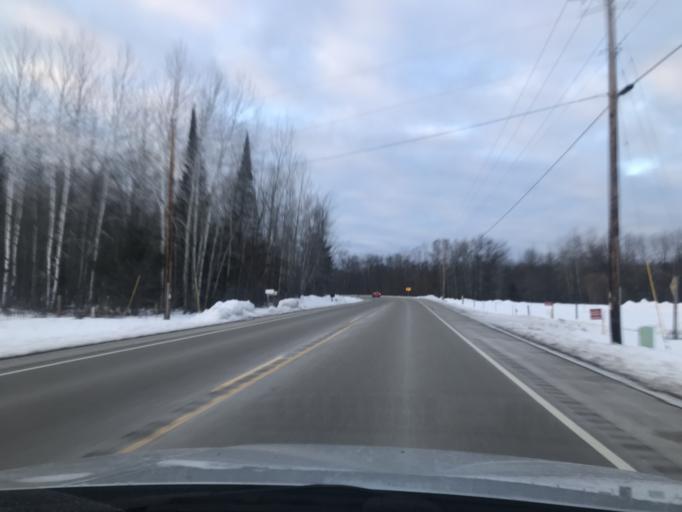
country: US
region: Wisconsin
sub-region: Marinette County
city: Marinette
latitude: 45.1391
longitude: -87.6909
